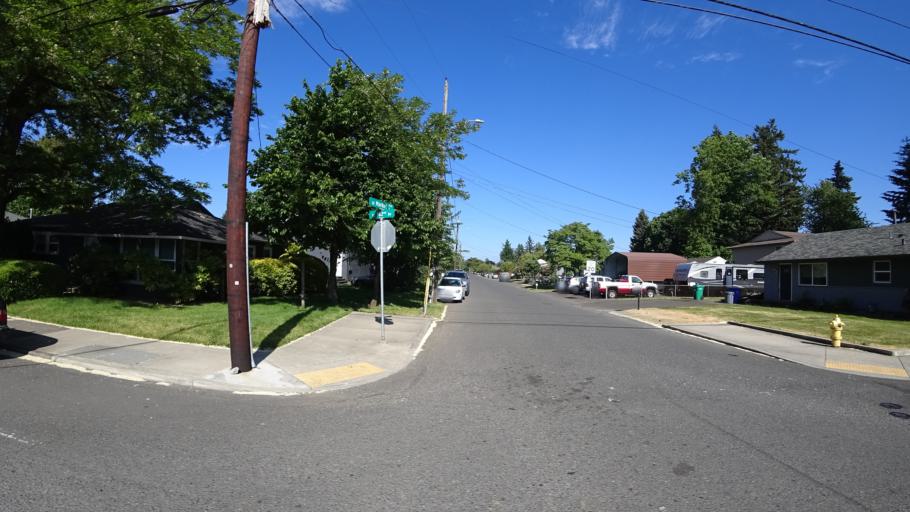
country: US
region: Oregon
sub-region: Multnomah County
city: Gresham
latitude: 45.5123
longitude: -122.4965
